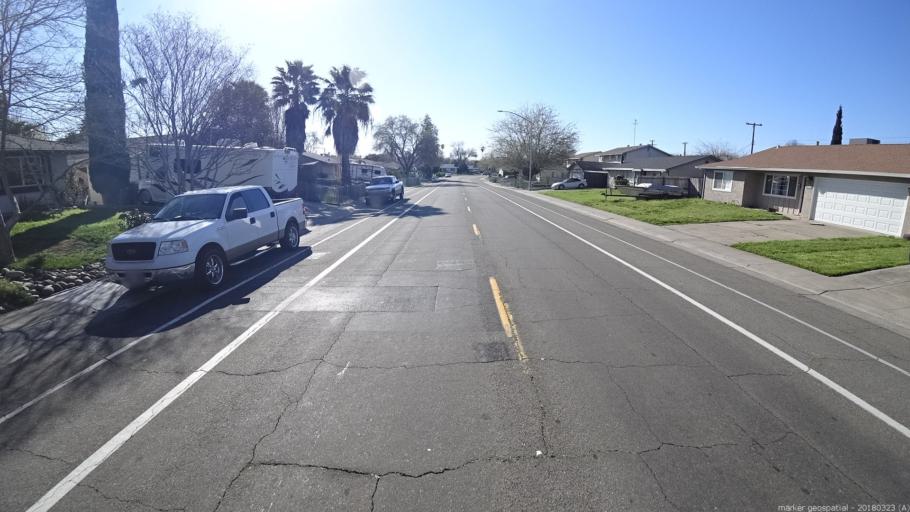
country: US
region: California
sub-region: Sacramento County
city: North Highlands
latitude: 38.7000
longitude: -121.3769
